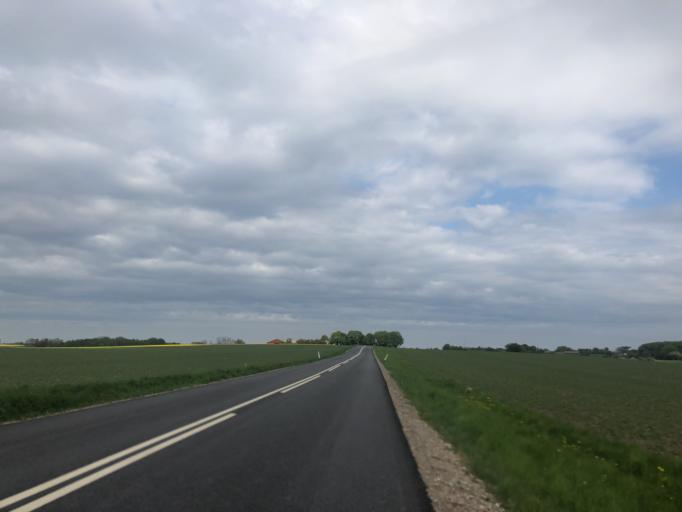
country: DK
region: Zealand
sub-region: Koge Kommune
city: Ejby
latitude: 55.4715
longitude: 12.1315
